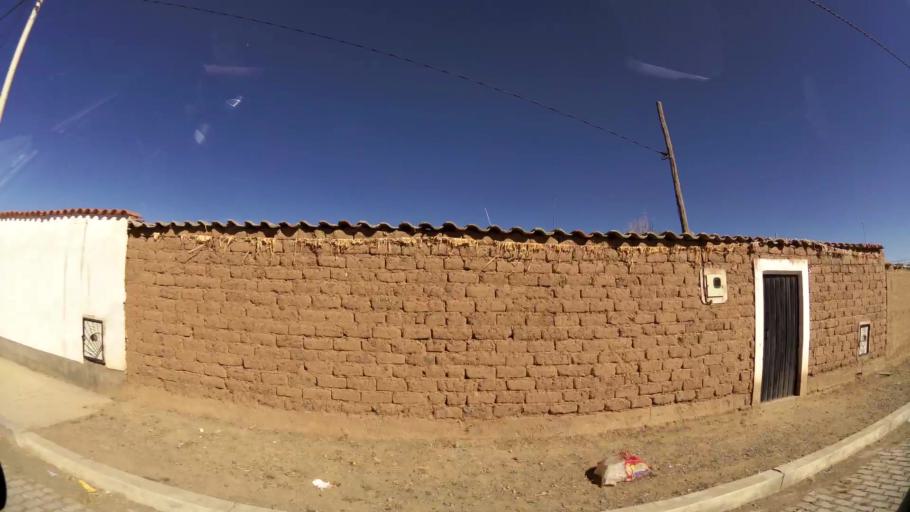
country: BO
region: La Paz
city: La Paz
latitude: -16.5341
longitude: -68.2260
